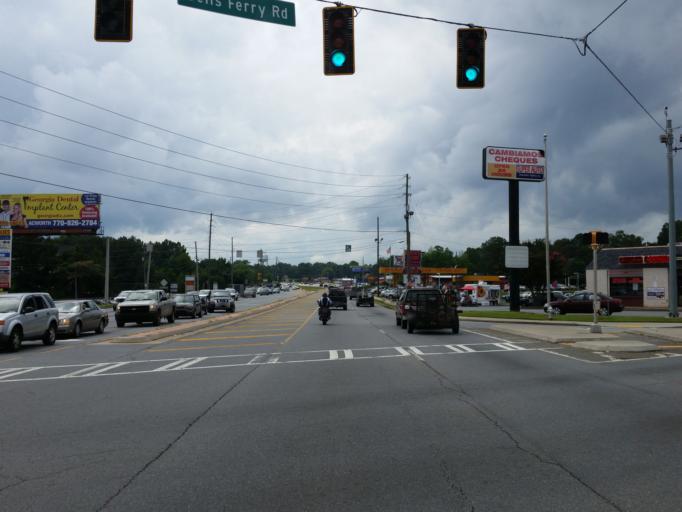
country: US
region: Georgia
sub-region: Cherokee County
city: Woodstock
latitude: 34.0881
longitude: -84.5772
